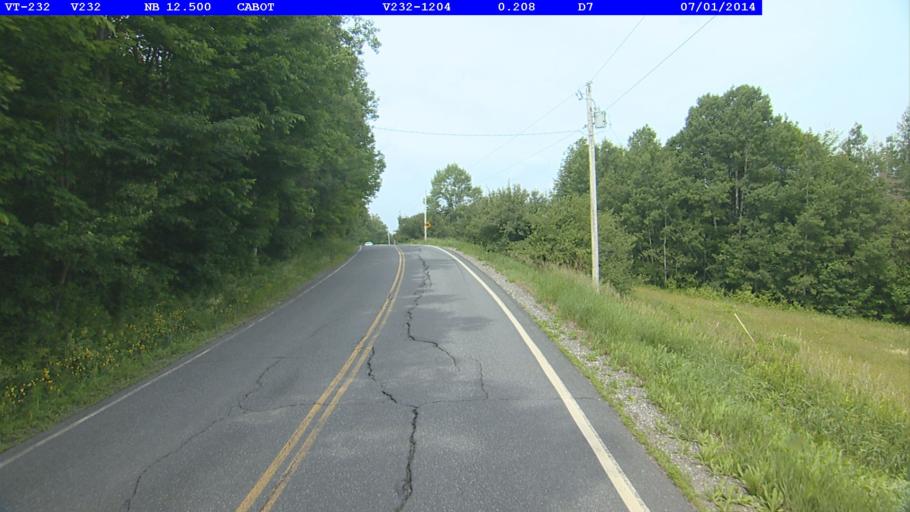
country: US
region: Vermont
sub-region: Caledonia County
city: Hardwick
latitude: 44.3567
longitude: -72.3092
